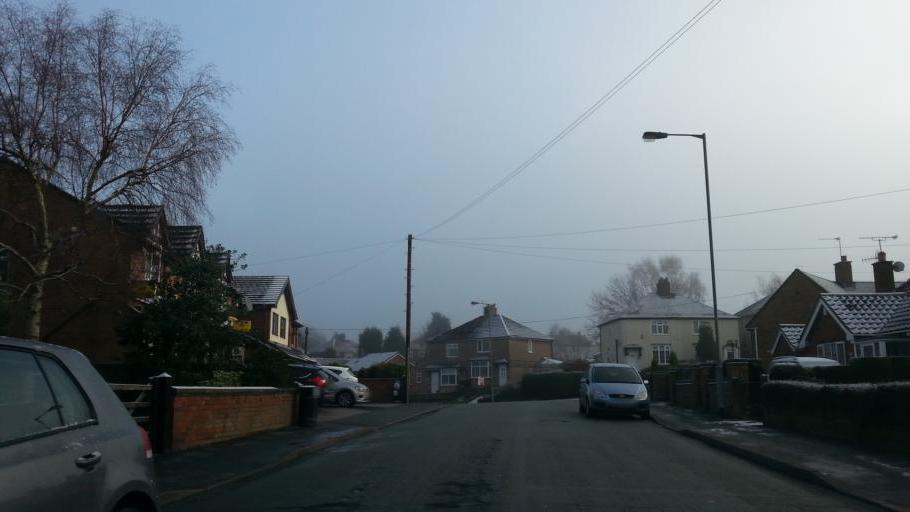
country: GB
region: England
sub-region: Staffordshire
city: Biddulph
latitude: 53.1242
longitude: -2.1677
